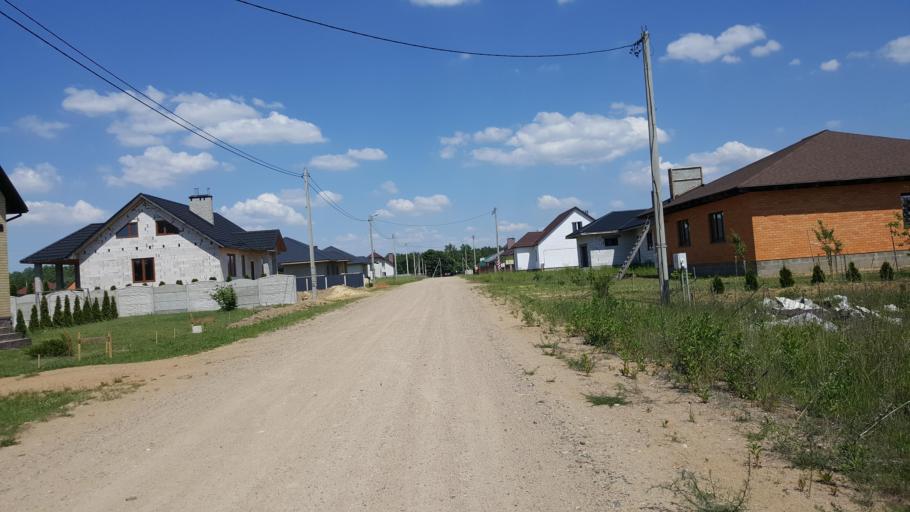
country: BY
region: Brest
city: Zhabinka
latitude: 52.1991
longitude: 24.0623
